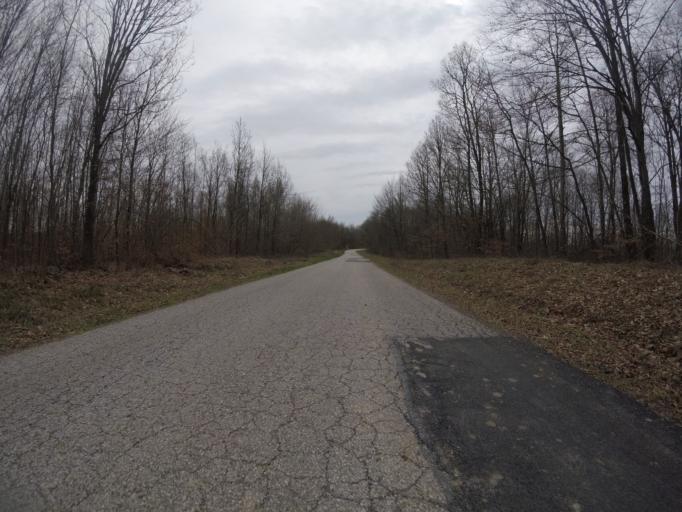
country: HR
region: Zagrebacka
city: Lukavec
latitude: 45.5855
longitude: 15.9630
